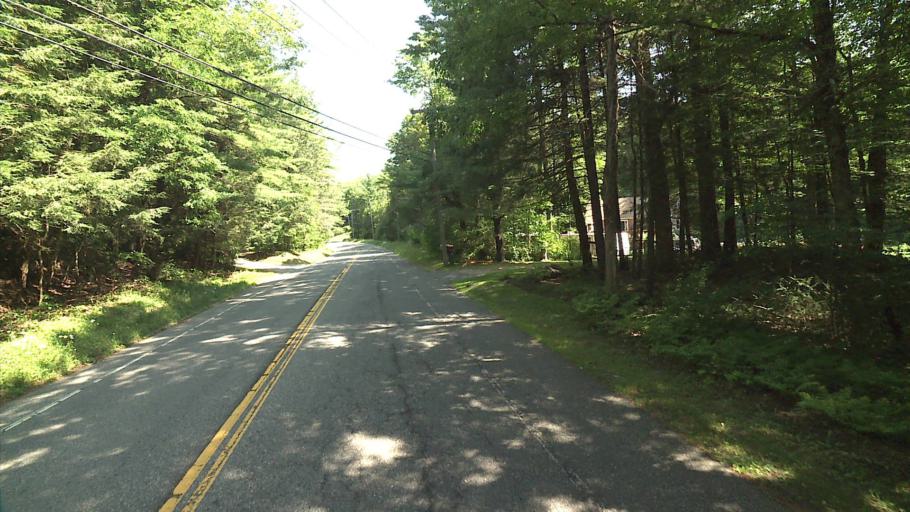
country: US
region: Connecticut
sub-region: Litchfield County
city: Winchester Center
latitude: 41.9657
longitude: -73.1994
